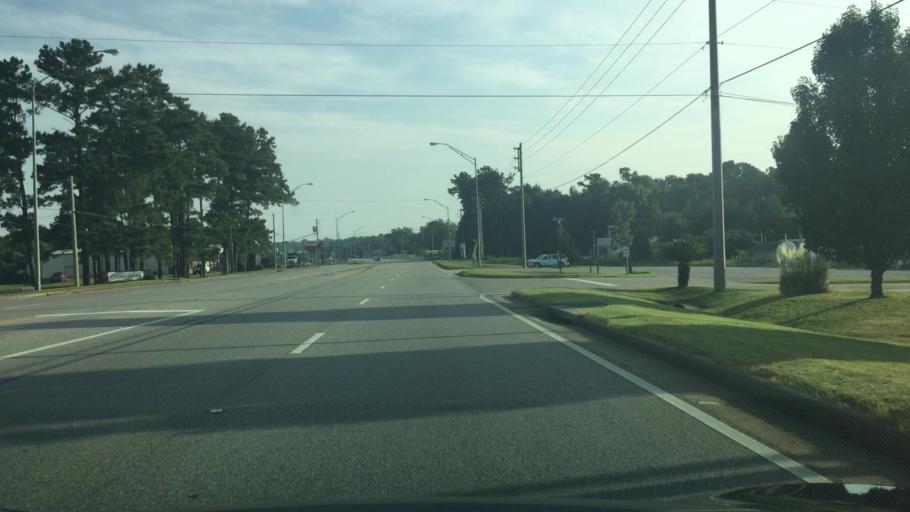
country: US
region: Alabama
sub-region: Covington County
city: Andalusia
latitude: 31.2964
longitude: -86.5003
